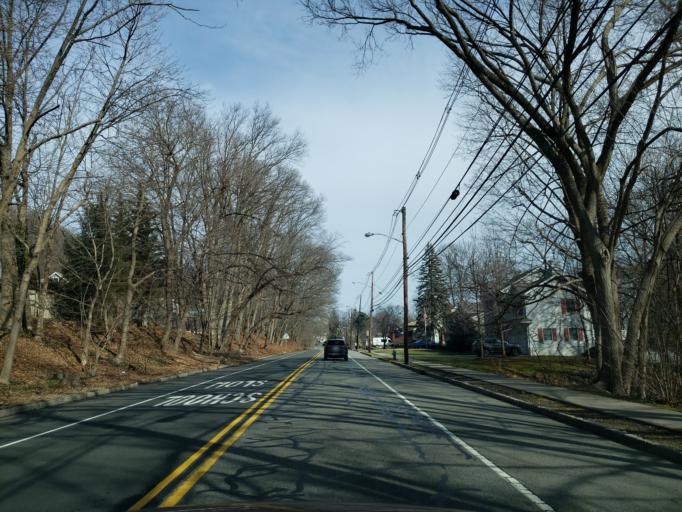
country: US
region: New Jersey
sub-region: Essex County
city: Verona
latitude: 40.8431
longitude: -74.2476
